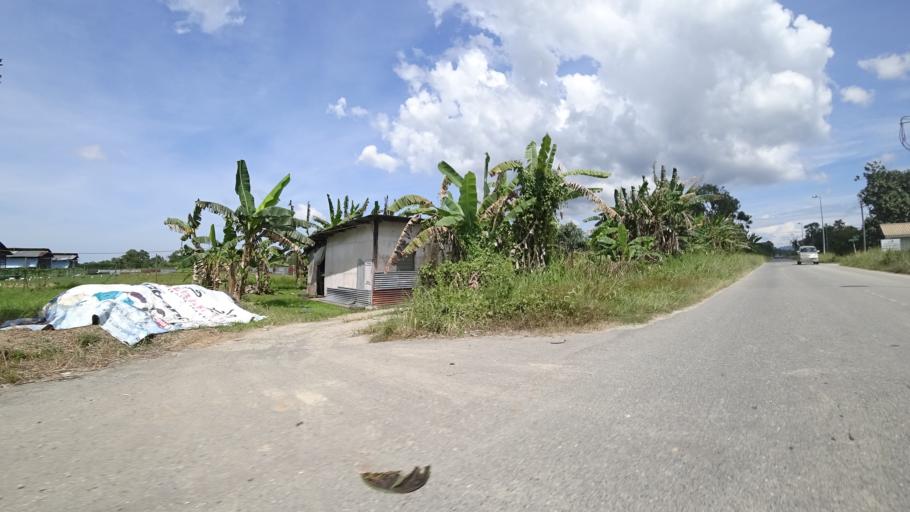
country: BN
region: Brunei and Muara
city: Bandar Seri Begawan
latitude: 4.8443
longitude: 114.8538
